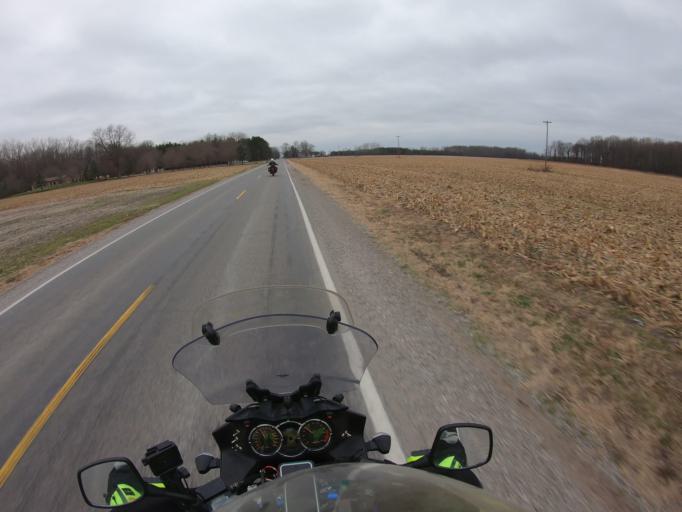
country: US
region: Michigan
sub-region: Saginaw County
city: Burt
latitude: 43.2558
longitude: -84.0118
